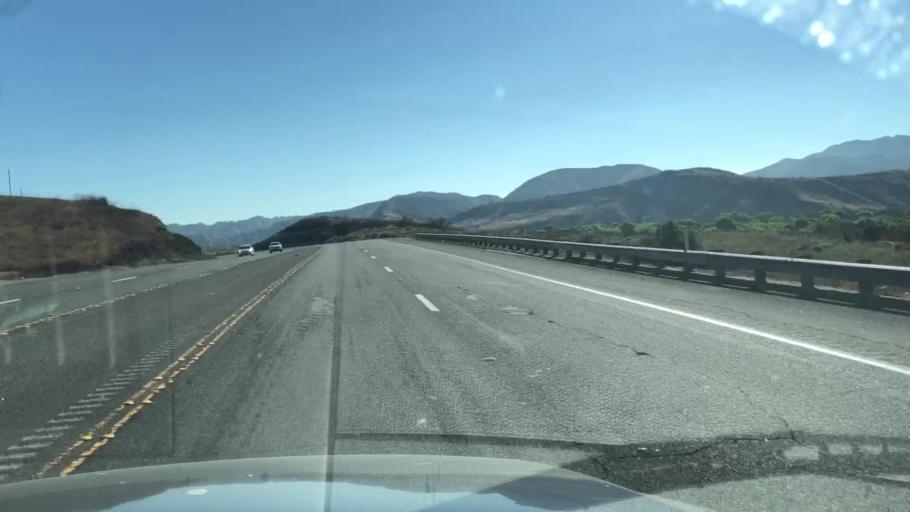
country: US
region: California
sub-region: Los Angeles County
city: Val Verde
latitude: 34.4078
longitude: -118.6818
